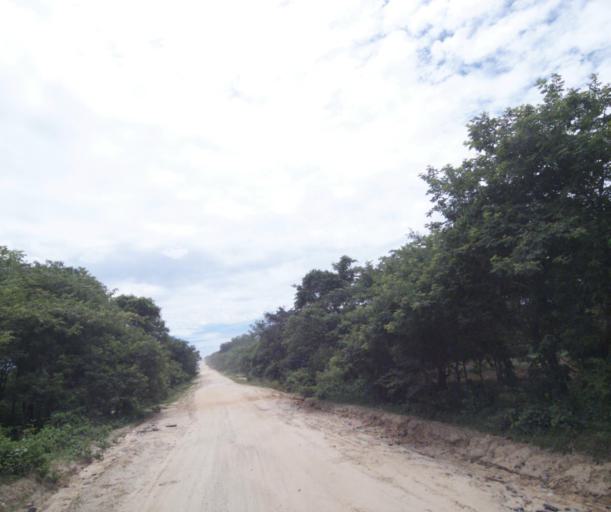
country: BR
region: Bahia
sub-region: Carinhanha
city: Carinhanha
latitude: -14.2123
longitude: -43.8980
